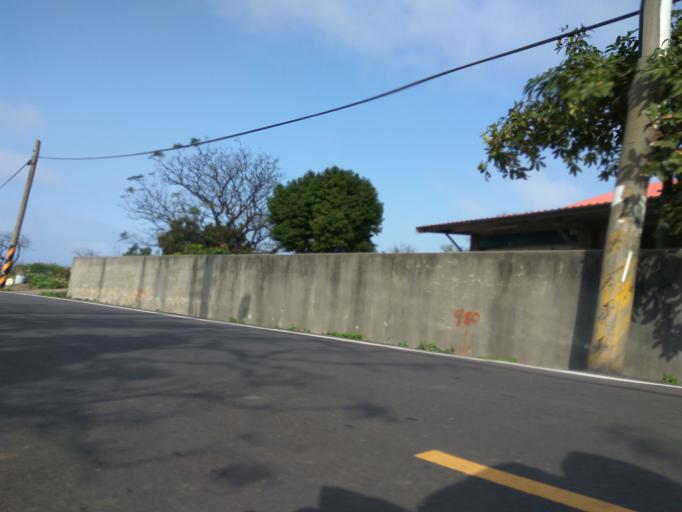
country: TW
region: Taiwan
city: Taoyuan City
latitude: 25.0698
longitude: 121.1726
